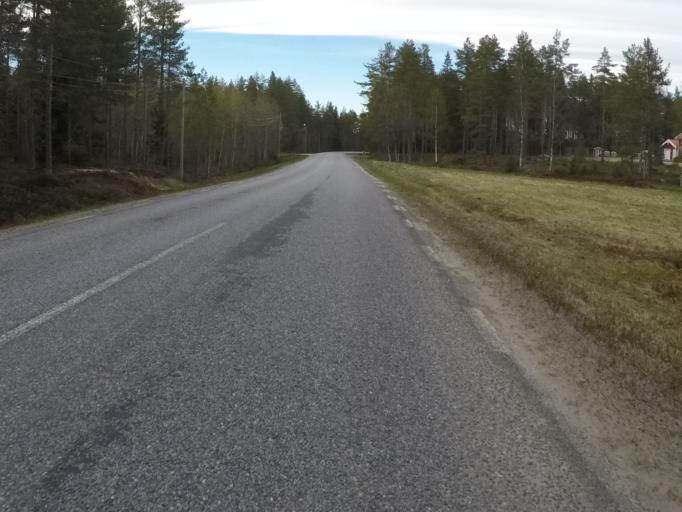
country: SE
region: Vaesterbotten
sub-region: Robertsfors Kommun
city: Robertsfors
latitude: 63.9617
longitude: 20.8087
